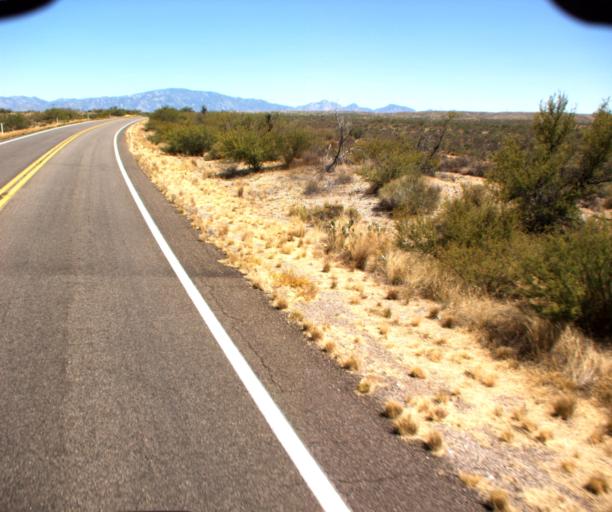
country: US
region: Arizona
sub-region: Pima County
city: Catalina
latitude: 32.6457
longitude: -111.0203
